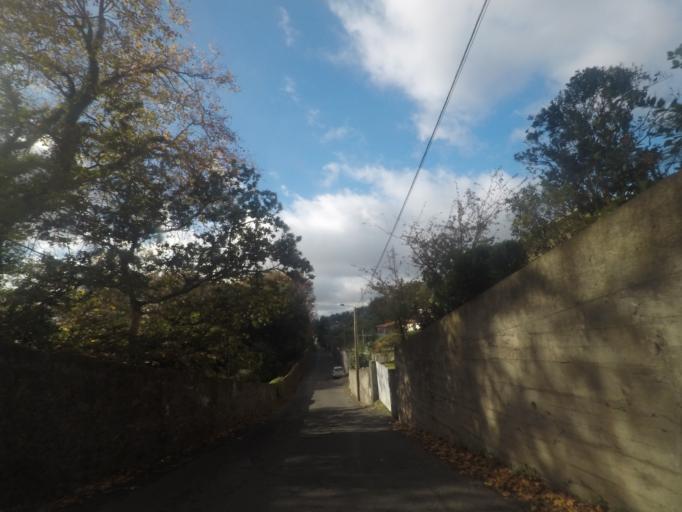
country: PT
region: Madeira
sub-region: Santa Cruz
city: Camacha
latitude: 32.6626
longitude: -16.8662
